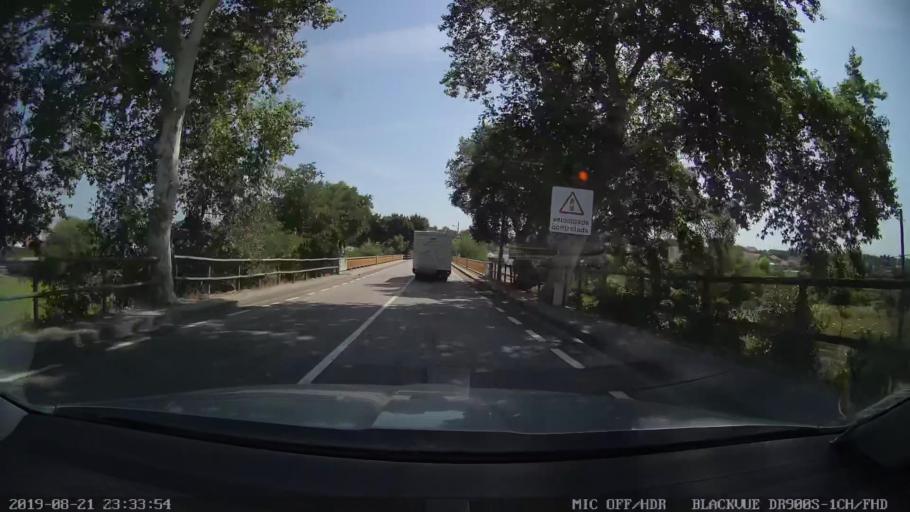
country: PT
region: Guarda
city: Alcains
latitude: 39.8835
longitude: -7.3995
